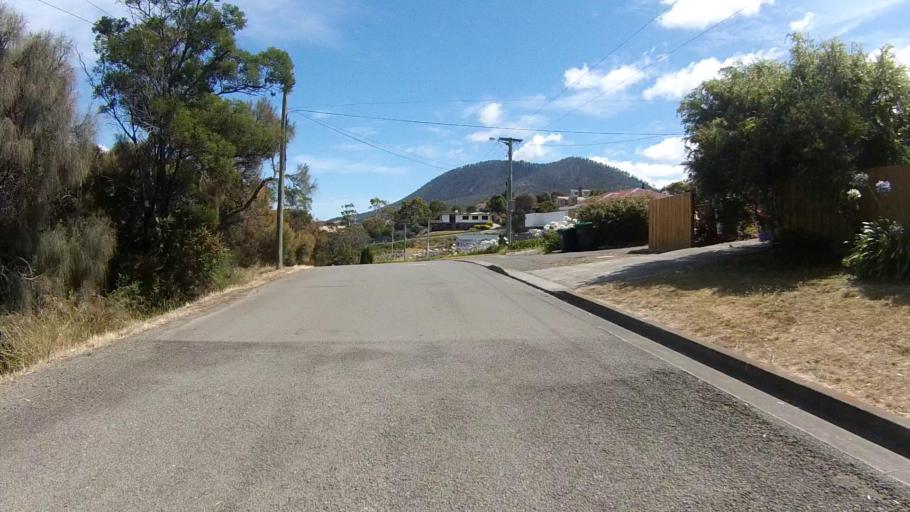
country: AU
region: Tasmania
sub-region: Glenorchy
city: Lutana
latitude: -42.8264
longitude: 147.3206
